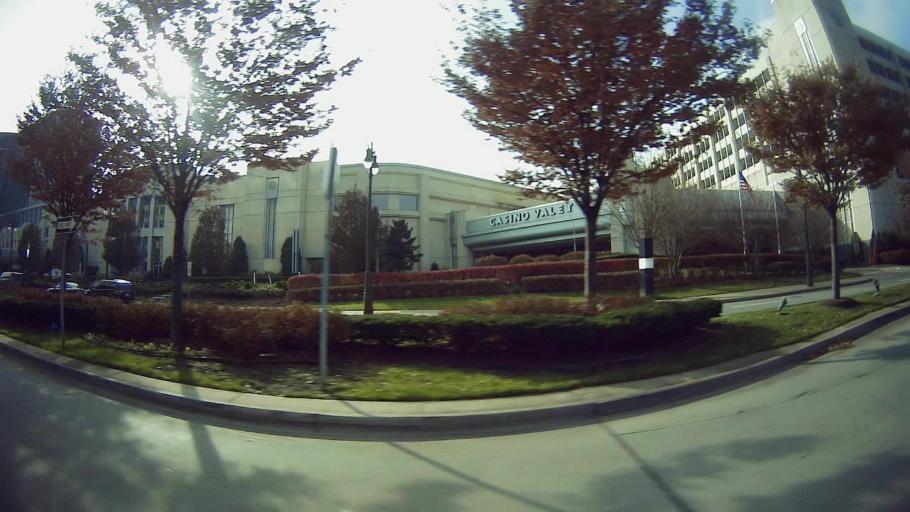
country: US
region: Michigan
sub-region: Wayne County
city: Detroit
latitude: 42.3345
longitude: -83.0589
